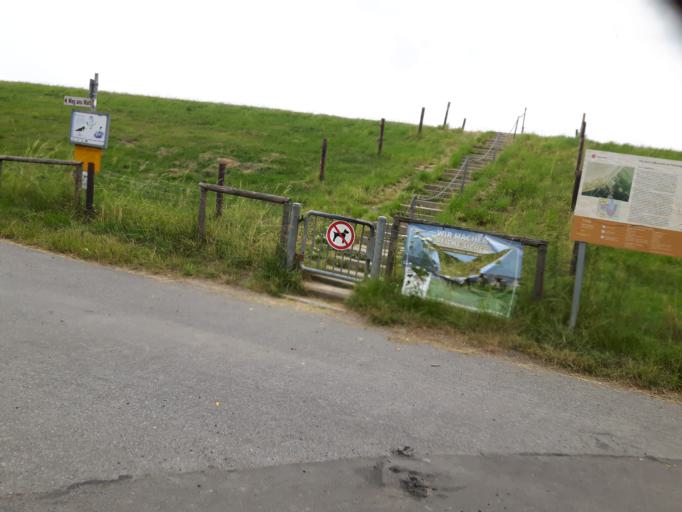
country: DE
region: Lower Saxony
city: Varel
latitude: 53.3952
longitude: 8.2605
